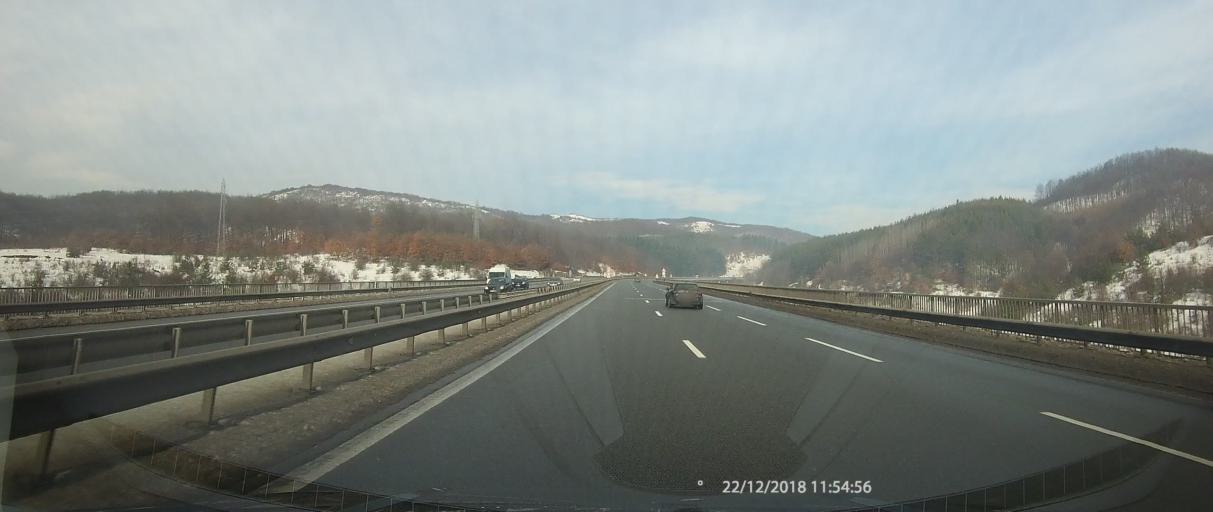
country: BG
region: Pernik
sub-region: Obshtina Pernik
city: Pernik
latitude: 42.6486
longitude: 23.1312
